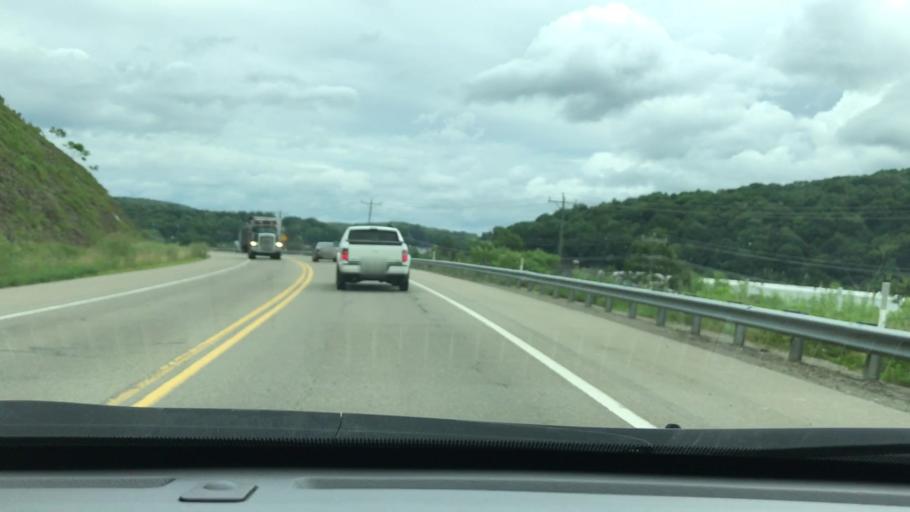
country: US
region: Pennsylvania
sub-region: Elk County
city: Johnsonburg
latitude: 41.4913
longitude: -78.6810
